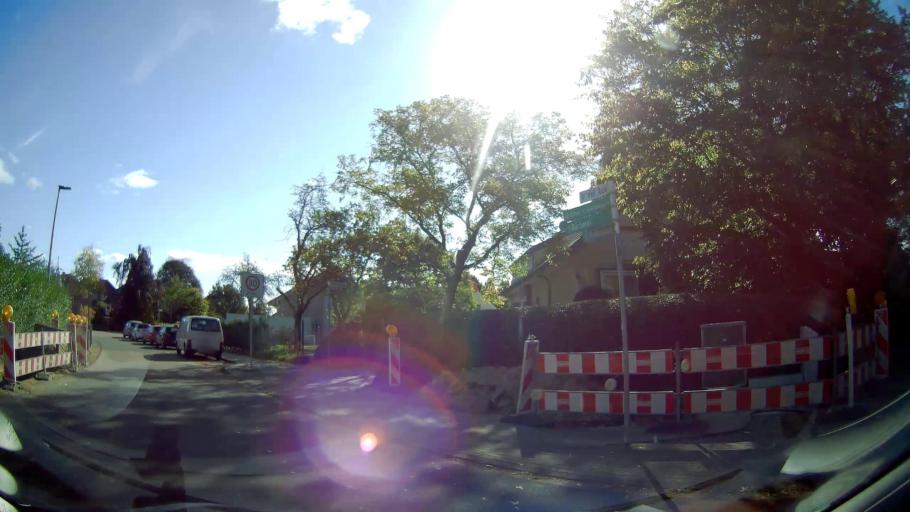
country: DE
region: North Rhine-Westphalia
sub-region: Regierungsbezirk Dusseldorf
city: Hunxe
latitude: 51.6380
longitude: 6.7653
